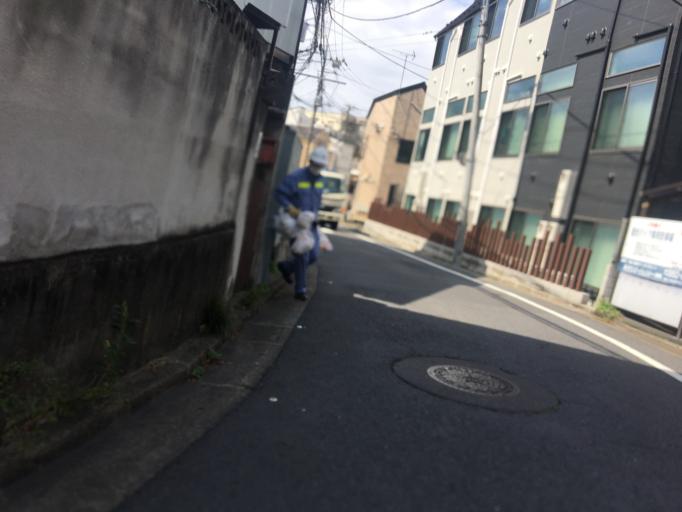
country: JP
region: Tokyo
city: Tokyo
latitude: 35.7111
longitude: 139.6807
